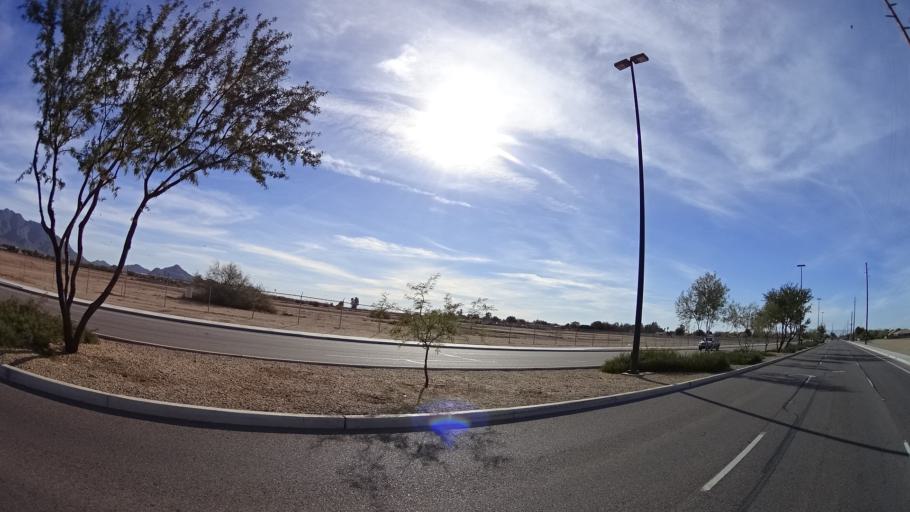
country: US
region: Arizona
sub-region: Maricopa County
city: Queen Creek
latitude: 33.2193
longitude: -111.7437
